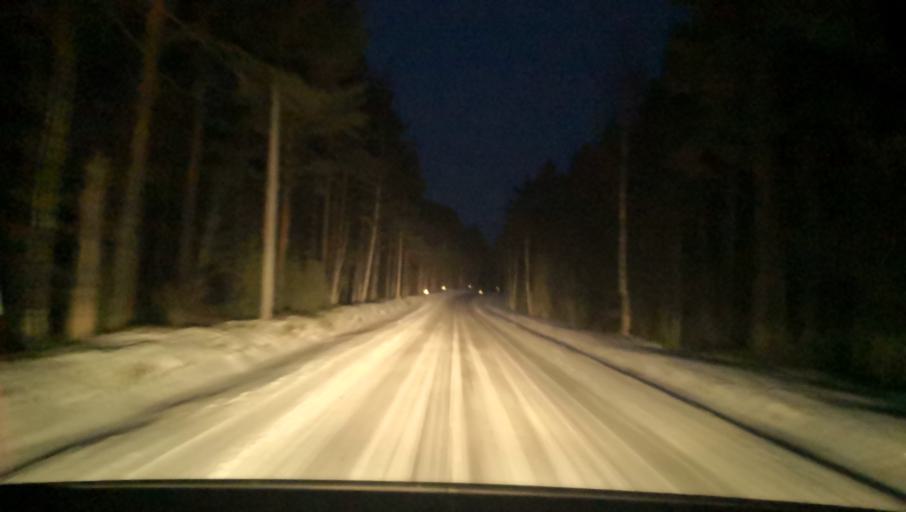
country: SE
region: Uppsala
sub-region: Heby Kommun
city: Tarnsjo
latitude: 60.2910
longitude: 16.8056
